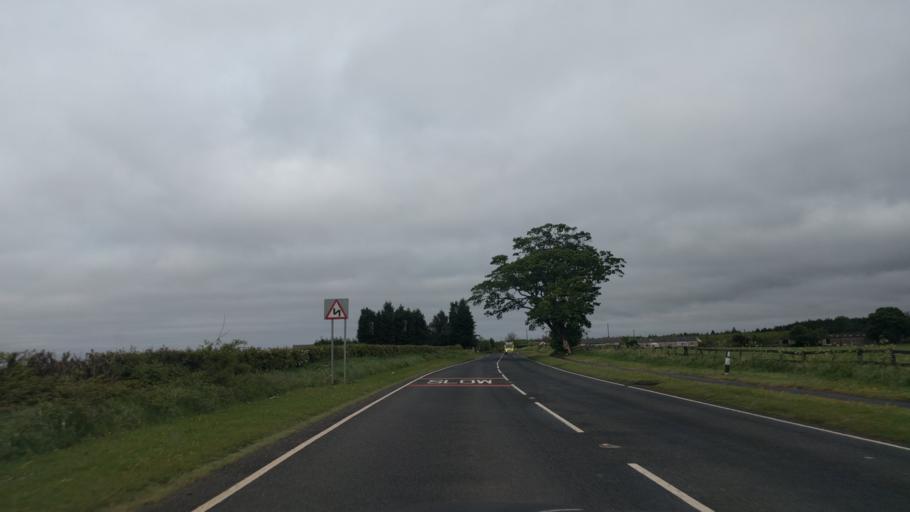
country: GB
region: England
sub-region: Northumberland
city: Pegswood
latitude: 55.1621
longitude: -1.6295
